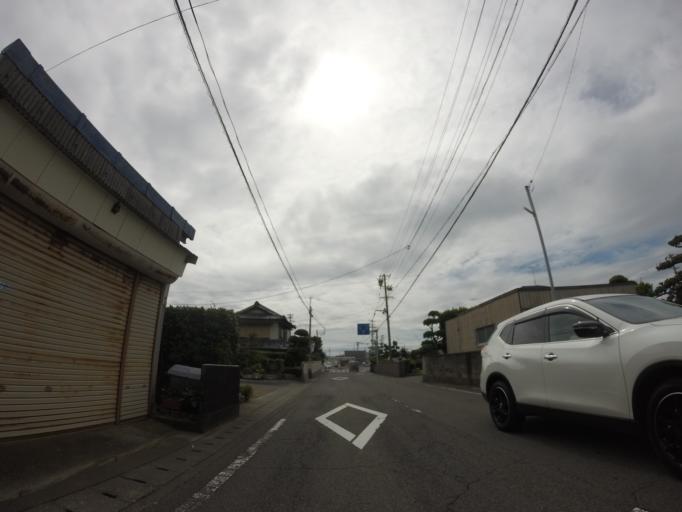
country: JP
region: Shizuoka
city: Oyama
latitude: 34.6103
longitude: 138.2044
